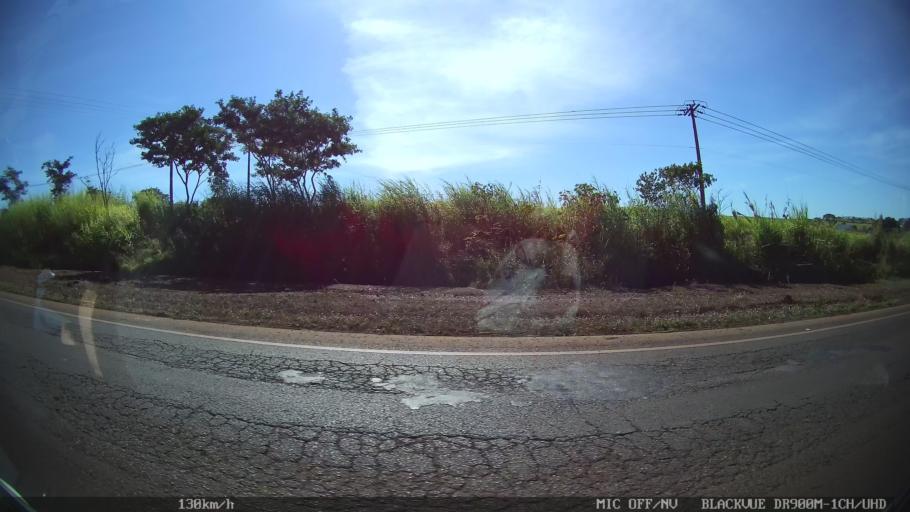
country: BR
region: Sao Paulo
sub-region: Ipua
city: Ipua
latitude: -20.4931
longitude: -48.0199
